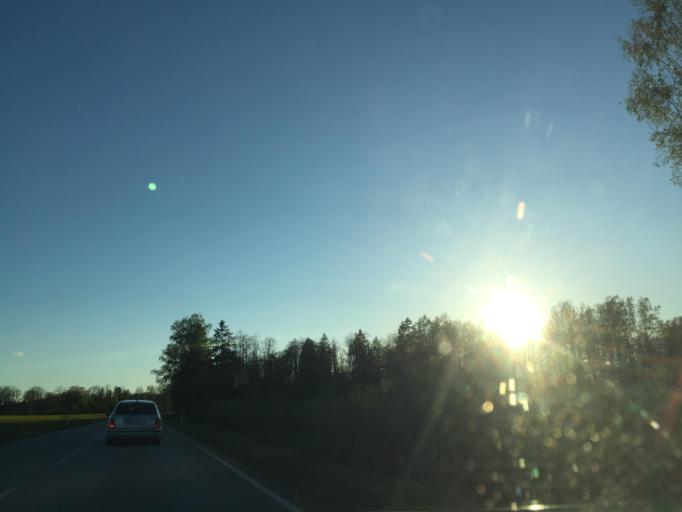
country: LV
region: Skriveri
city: Skriveri
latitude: 56.8824
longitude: 25.2496
